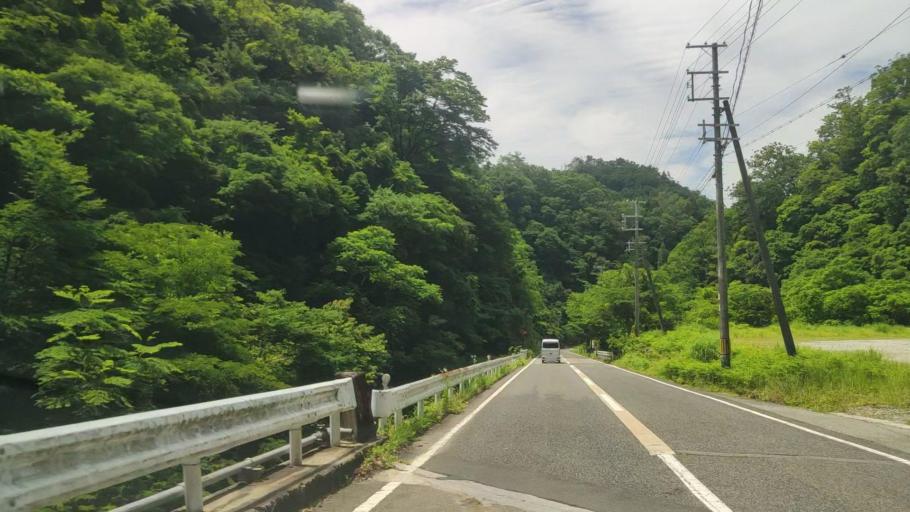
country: JP
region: Hyogo
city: Toyooka
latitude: 35.4783
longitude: 134.6059
